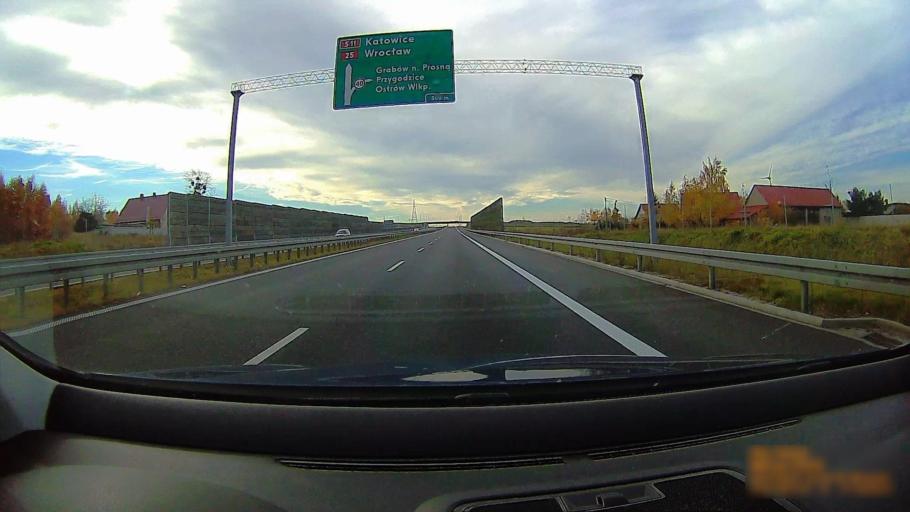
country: PL
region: Greater Poland Voivodeship
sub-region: Powiat ostrowski
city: Przygodzice
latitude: 51.6360
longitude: 17.8729
